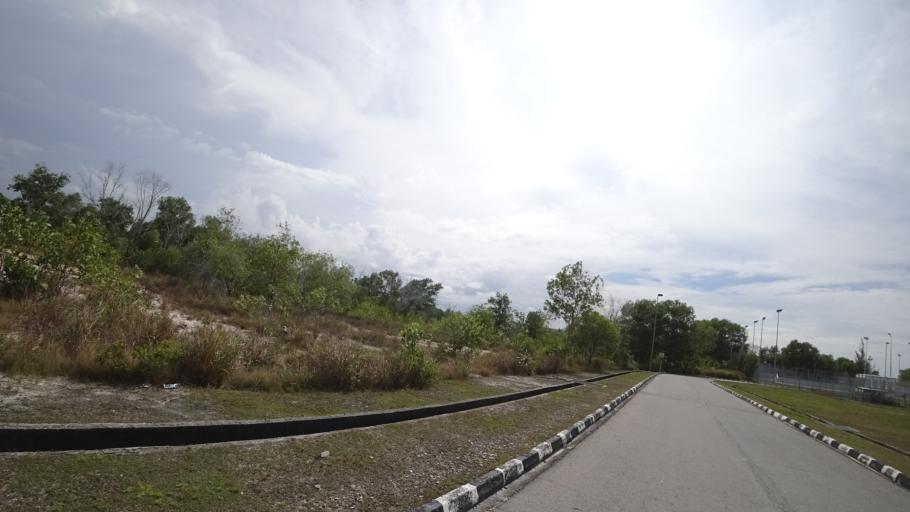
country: BN
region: Tutong
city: Tutong
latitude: 4.8119
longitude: 114.6593
